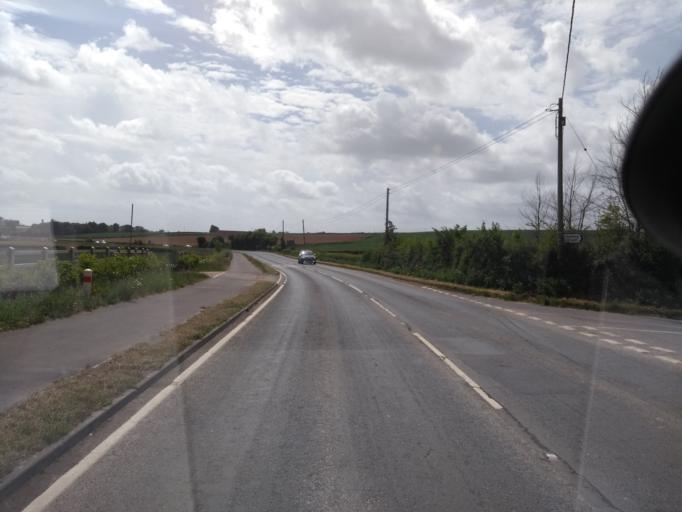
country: GB
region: England
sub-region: Somerset
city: Bridgwater
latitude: 51.1417
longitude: -3.0565
